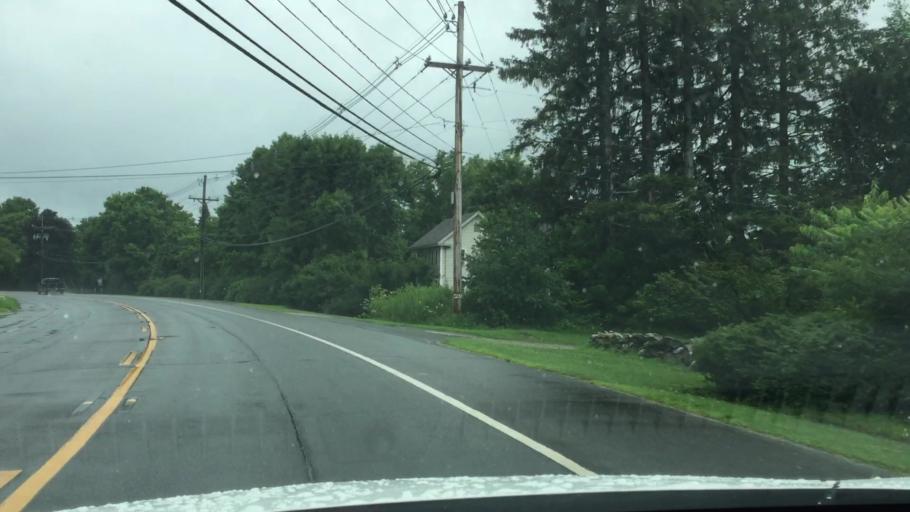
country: US
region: Massachusetts
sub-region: Berkshire County
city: Lanesborough
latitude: 42.5332
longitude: -73.2300
